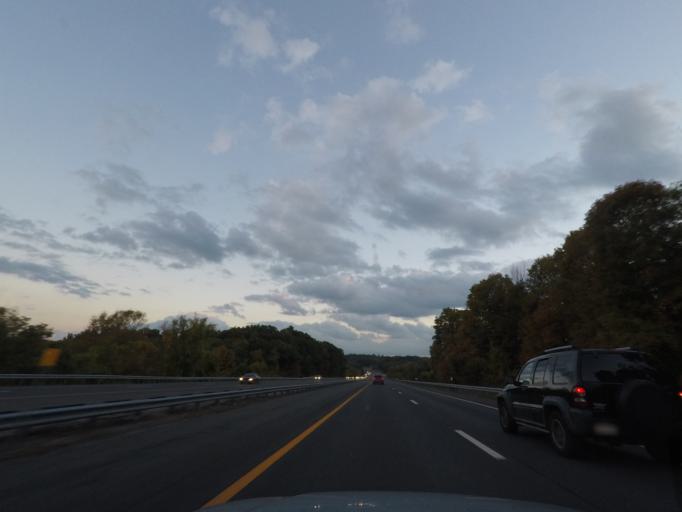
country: US
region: New York
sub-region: Ulster County
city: Rosendale Village
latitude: 41.8590
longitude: -74.0580
